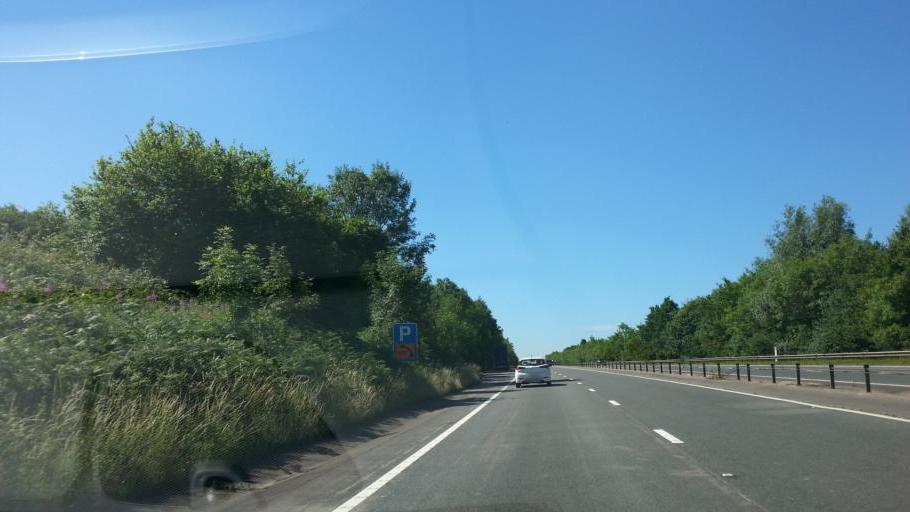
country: GB
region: Wales
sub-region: Newport
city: Langstone
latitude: 51.6184
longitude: -2.9085
